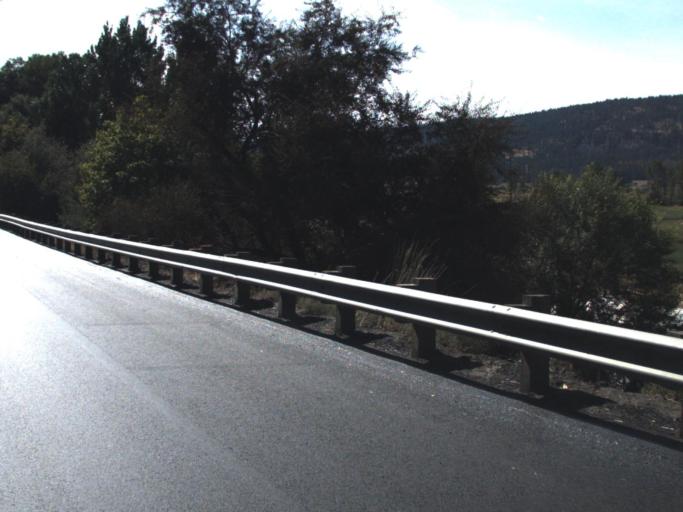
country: US
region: Washington
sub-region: Stevens County
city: Colville
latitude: 48.5242
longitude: -117.9029
